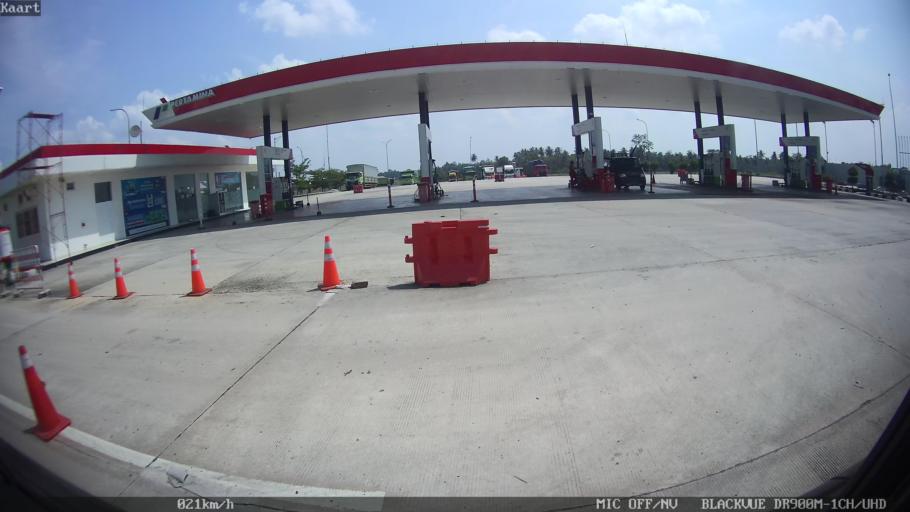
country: ID
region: Lampung
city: Kedaton
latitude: -5.3190
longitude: 105.2666
